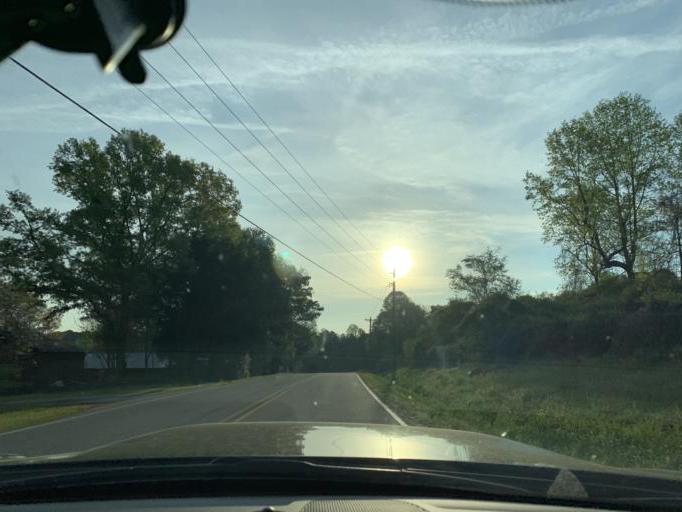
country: US
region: Georgia
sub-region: Forsyth County
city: Cumming
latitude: 34.2588
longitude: -84.1563
